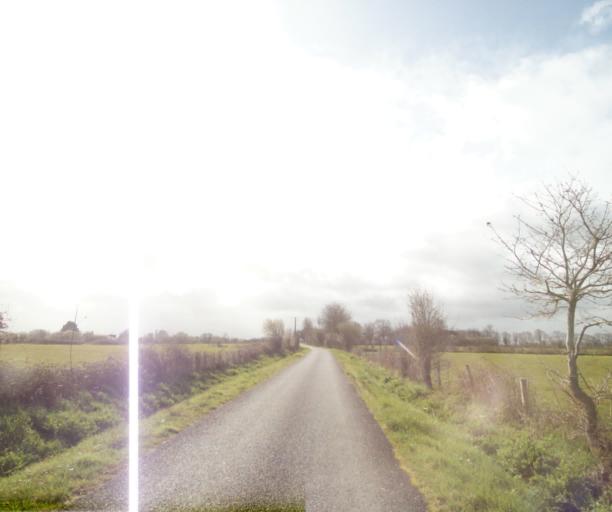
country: FR
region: Pays de la Loire
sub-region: Departement de la Loire-Atlantique
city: Bouvron
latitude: 47.4129
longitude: -1.8565
